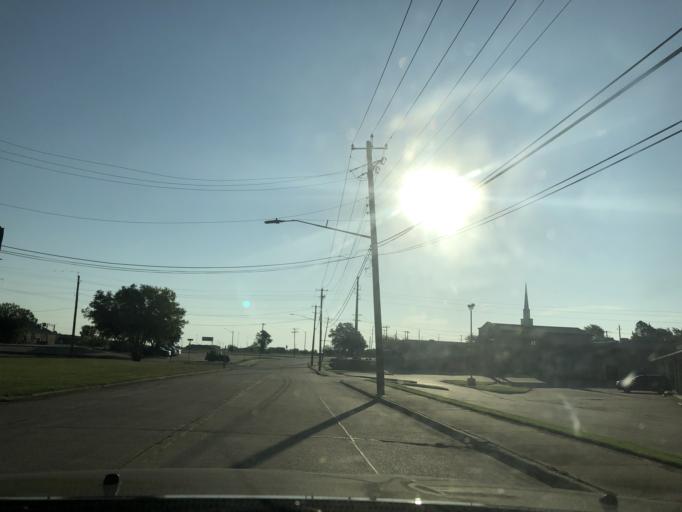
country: US
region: Texas
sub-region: Dallas County
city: Sunnyvale
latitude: 32.8479
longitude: -96.5715
